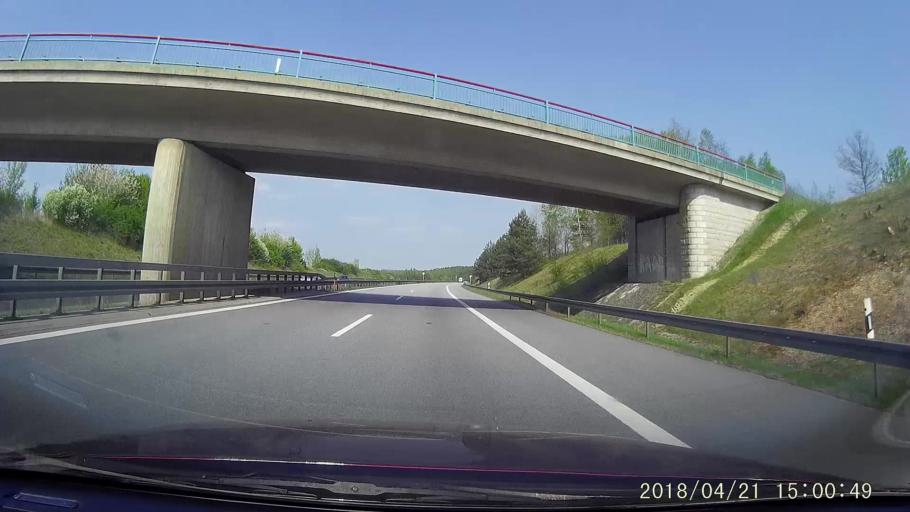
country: DE
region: Saxony
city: Reichenbach
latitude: 51.2126
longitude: 14.8002
